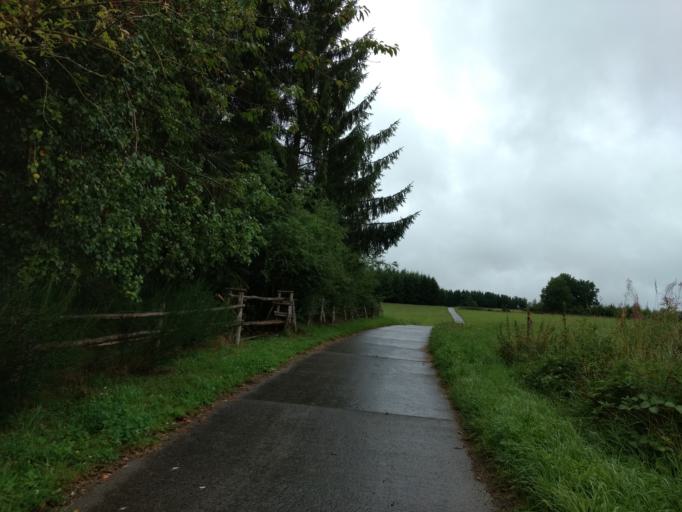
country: BE
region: Wallonia
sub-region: Province du Luxembourg
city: Houffalize
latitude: 50.1546
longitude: 5.7196
